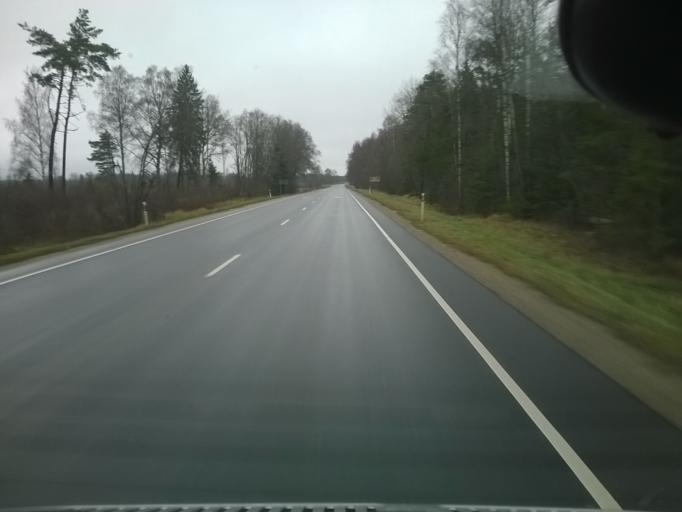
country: EE
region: Harju
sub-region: Nissi vald
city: Turba
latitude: 59.0131
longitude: 24.1352
